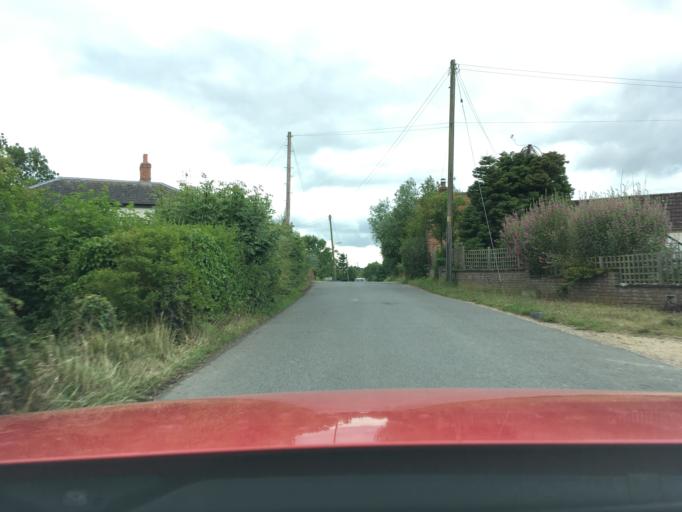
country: GB
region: England
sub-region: Gloucestershire
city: Stonehouse
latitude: 51.7887
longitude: -2.3624
